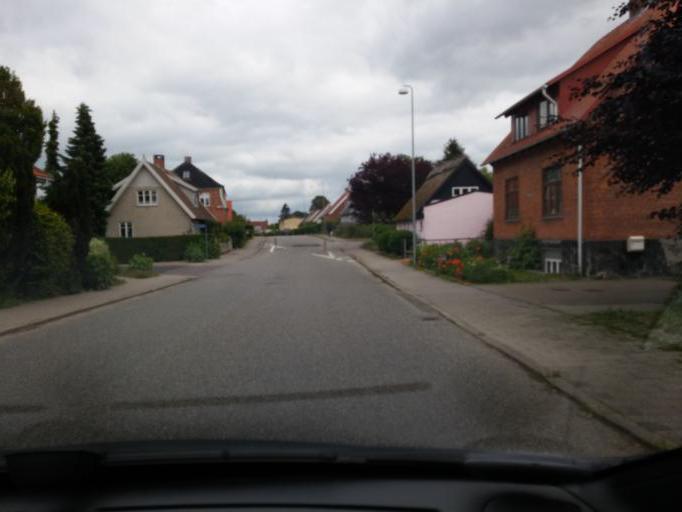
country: DK
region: Capital Region
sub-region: Hillerod Kommune
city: Hillerod
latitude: 55.9366
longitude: 12.3183
